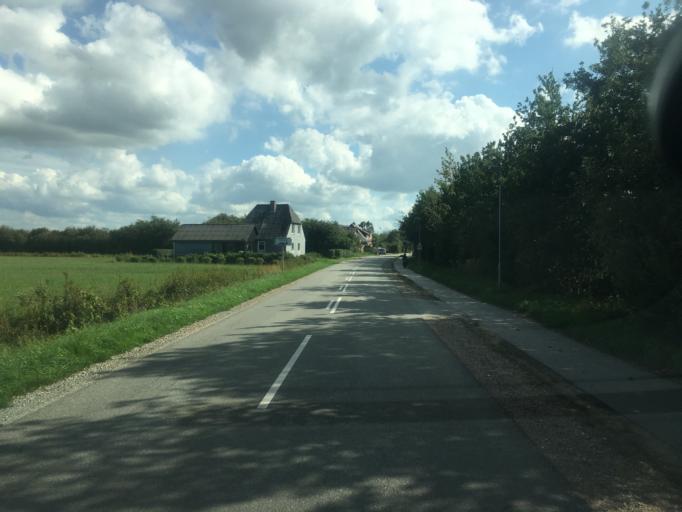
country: DE
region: Schleswig-Holstein
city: Ellhoft
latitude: 54.9428
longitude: 8.9678
